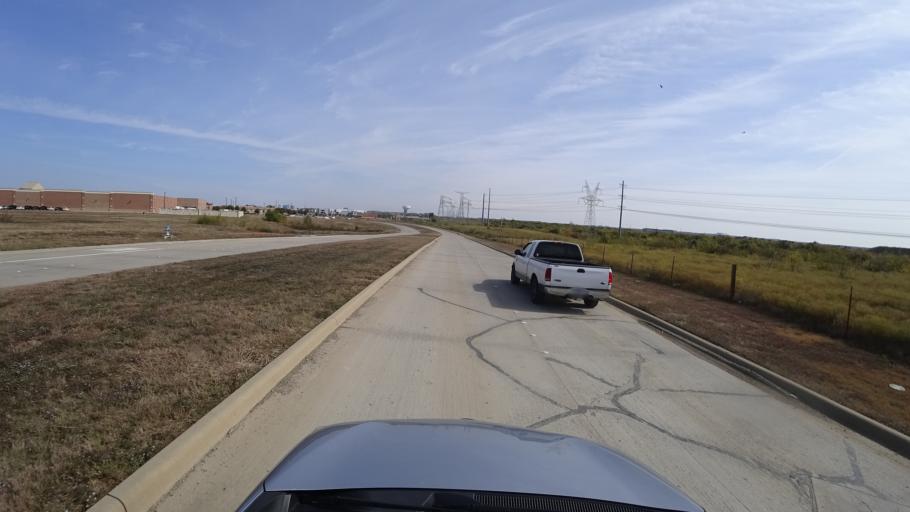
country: US
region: Texas
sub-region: Denton County
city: The Colony
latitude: 33.0604
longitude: -96.8912
